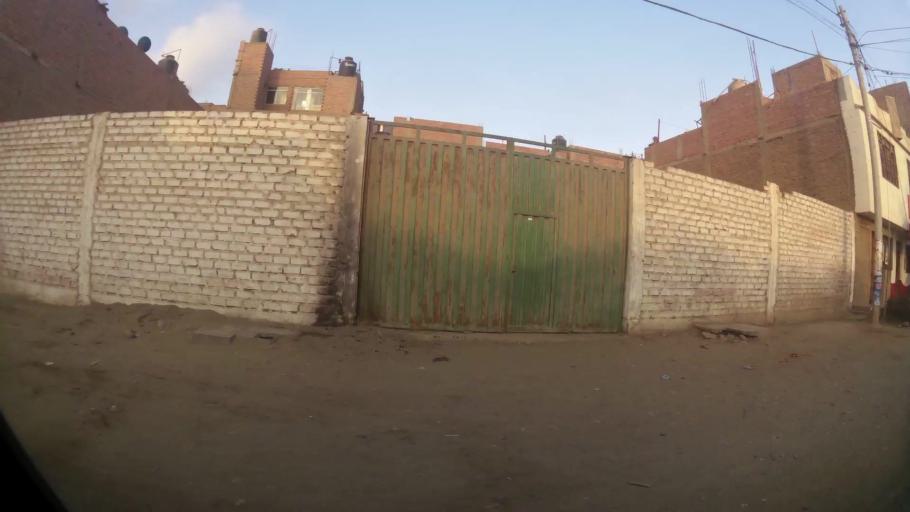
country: PE
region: Lima
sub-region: Huaura
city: Huacho
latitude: -11.1089
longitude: -77.5971
